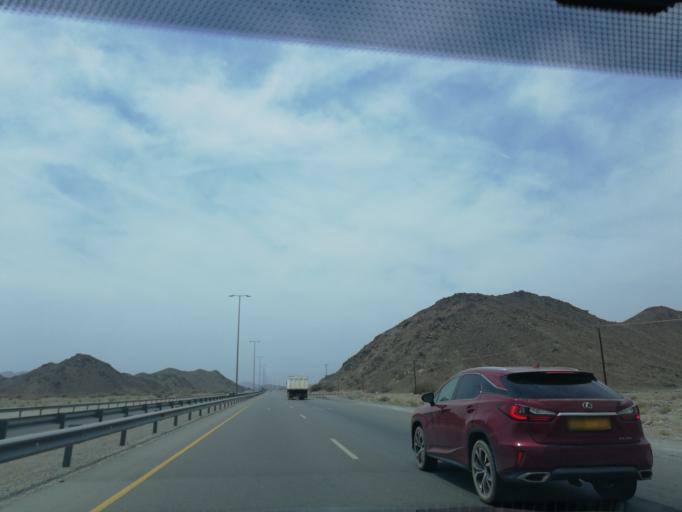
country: OM
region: Muhafazat ad Dakhiliyah
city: Bidbid
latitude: 23.3997
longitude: 58.0758
